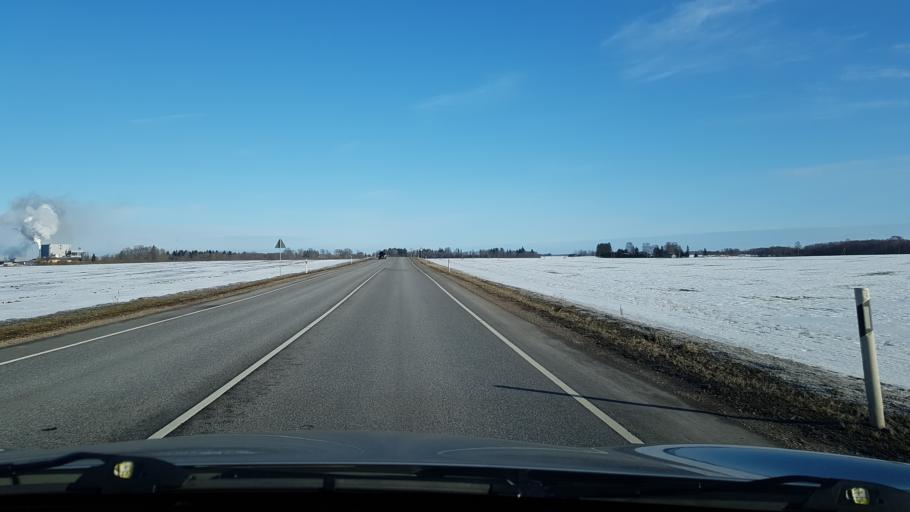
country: EE
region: Viljandimaa
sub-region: Vohma linn
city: Vohma
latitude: 58.7167
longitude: 25.7550
